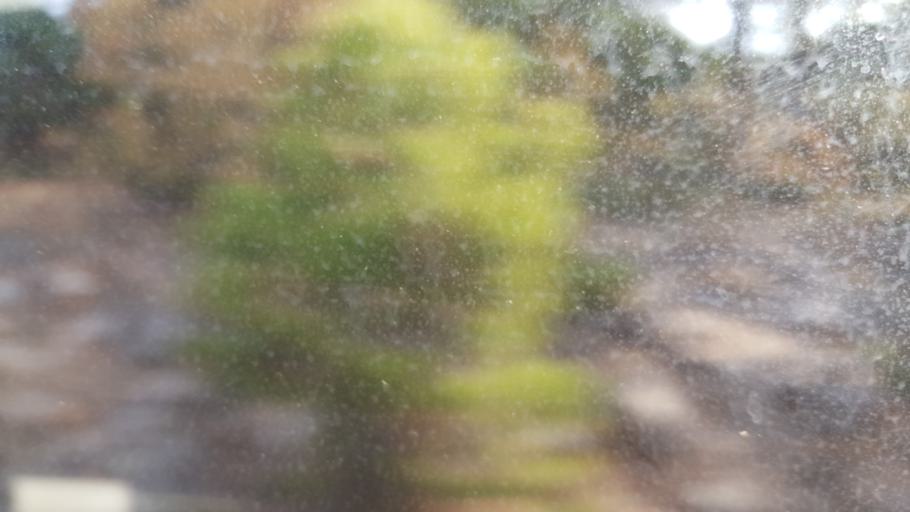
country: TR
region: Eskisehir
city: Mihaliccik
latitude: 39.9524
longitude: 31.3892
